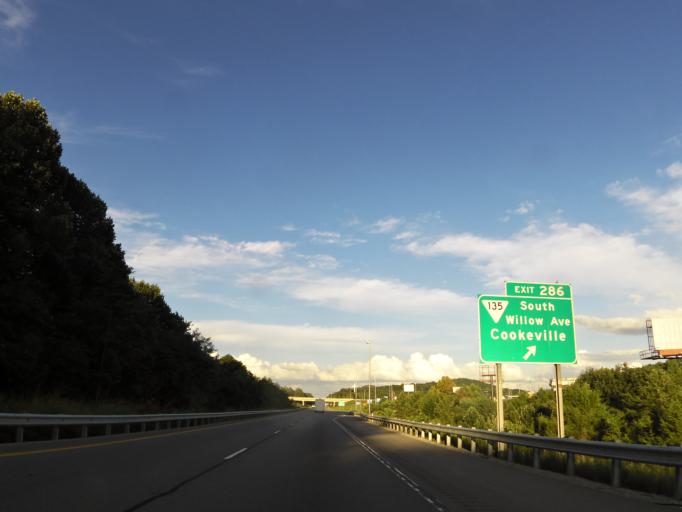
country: US
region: Tennessee
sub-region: Putnam County
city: Cookeville
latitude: 36.1368
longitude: -85.5352
